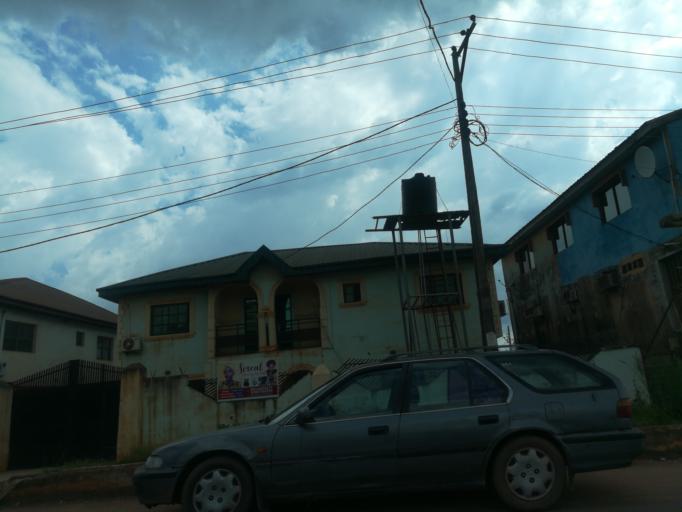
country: NG
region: Oyo
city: Ido
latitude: 7.4357
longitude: 3.8304
